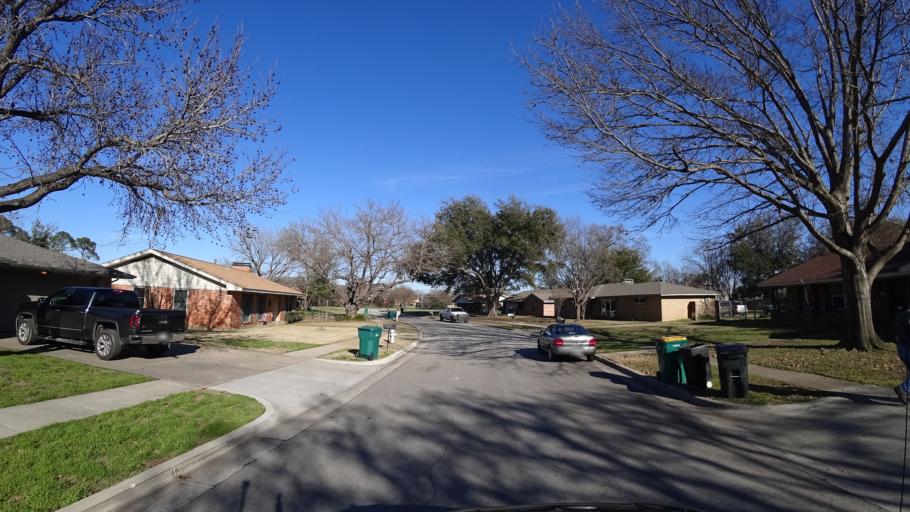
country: US
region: Texas
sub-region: Denton County
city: Lewisville
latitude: 33.0744
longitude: -97.0121
